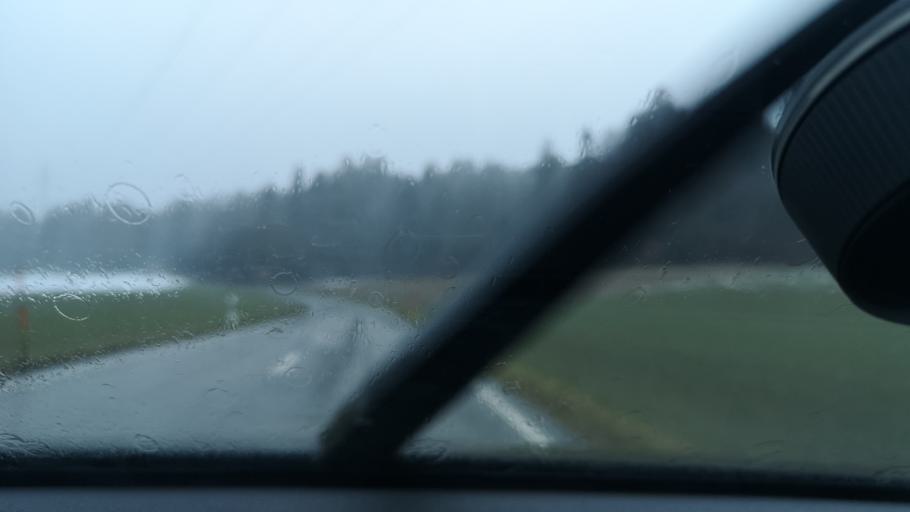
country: CH
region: Neuchatel
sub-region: Val-de-Ruz District
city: Les Geneveys-sur-Coffrane
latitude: 46.9842
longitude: 6.8487
